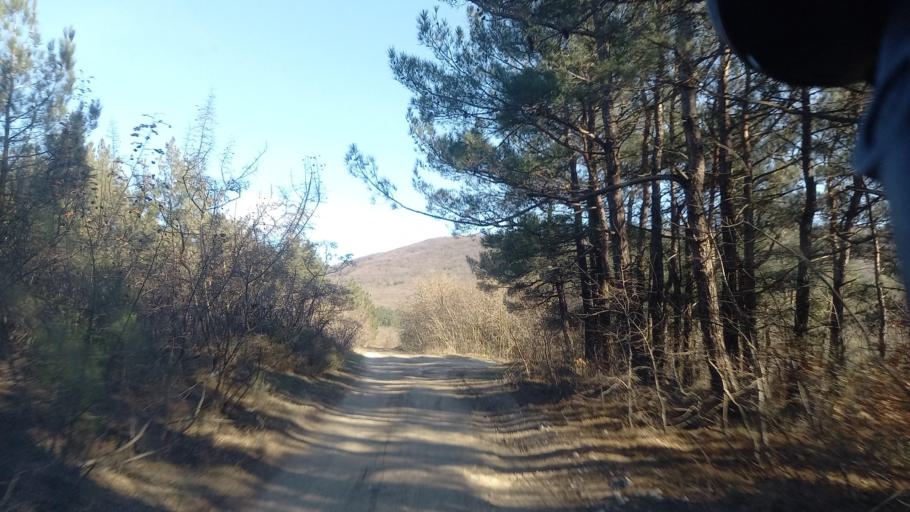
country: RU
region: Krasnodarskiy
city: Kabardinka
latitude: 44.6291
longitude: 37.9294
